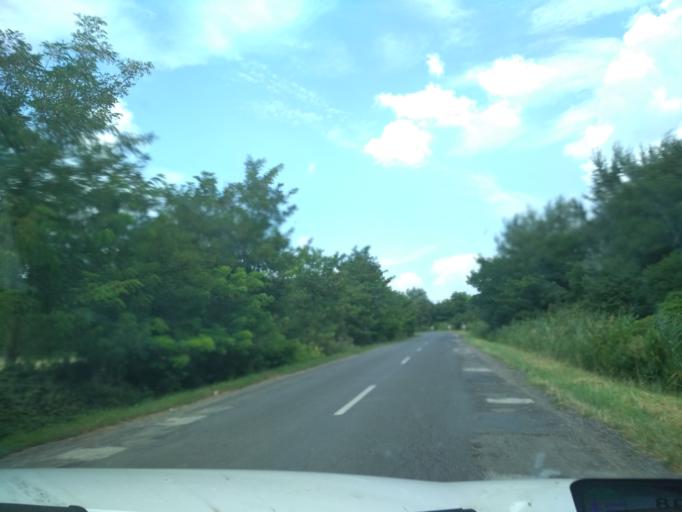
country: HU
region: Jasz-Nagykun-Szolnok
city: Tiszaszolos
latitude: 47.5252
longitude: 20.6867
